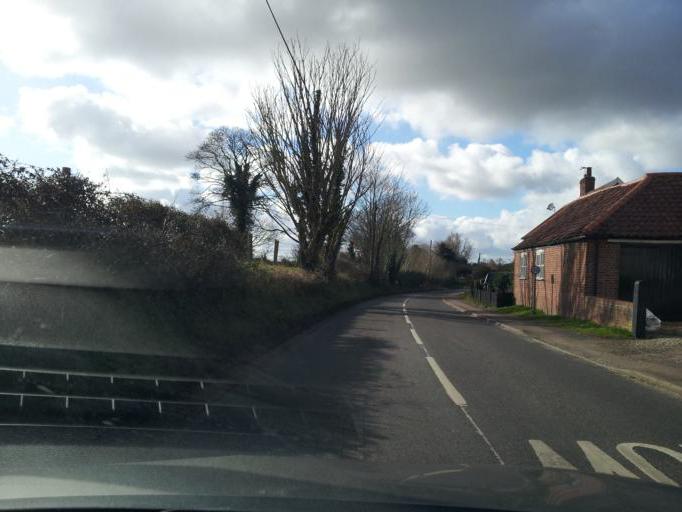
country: GB
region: England
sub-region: Norfolk
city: Mattishall
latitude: 52.6583
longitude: 0.9873
